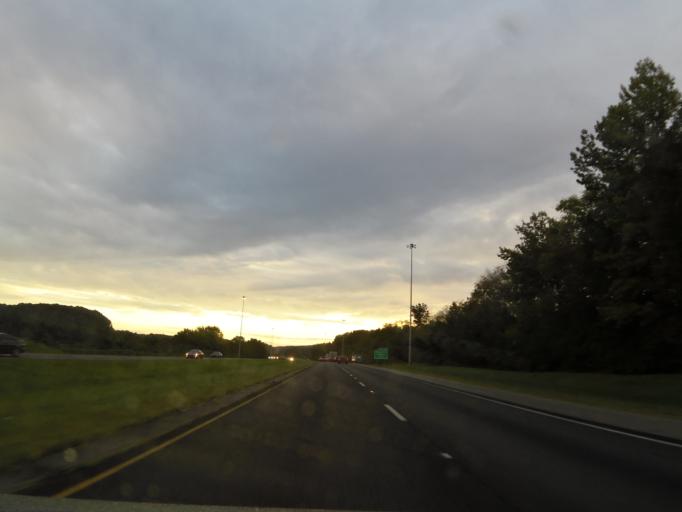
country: US
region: Alabama
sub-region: Jefferson County
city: Trussville
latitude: 33.6523
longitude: -86.6034
